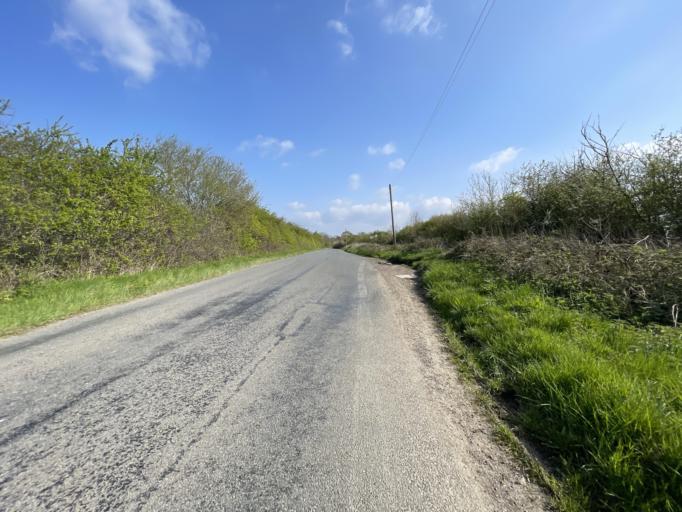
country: GB
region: England
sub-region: Warwickshire
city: Rugby
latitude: 52.3411
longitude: -1.2346
